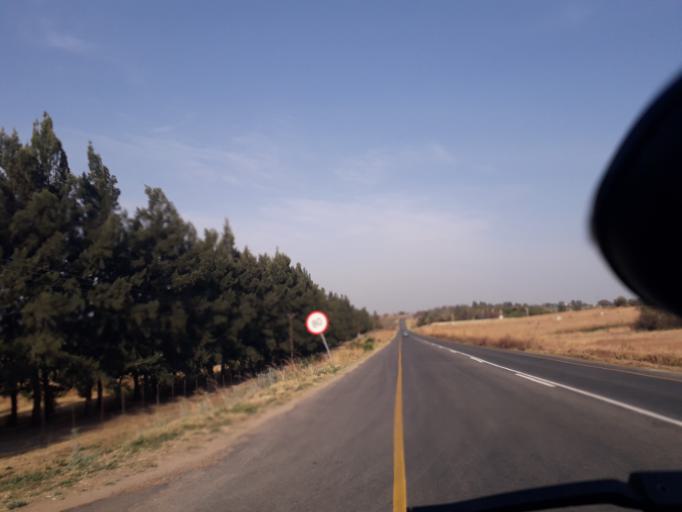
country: ZA
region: Gauteng
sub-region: West Rand District Municipality
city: Muldersdriseloop
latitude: -25.9604
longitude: 27.8881
